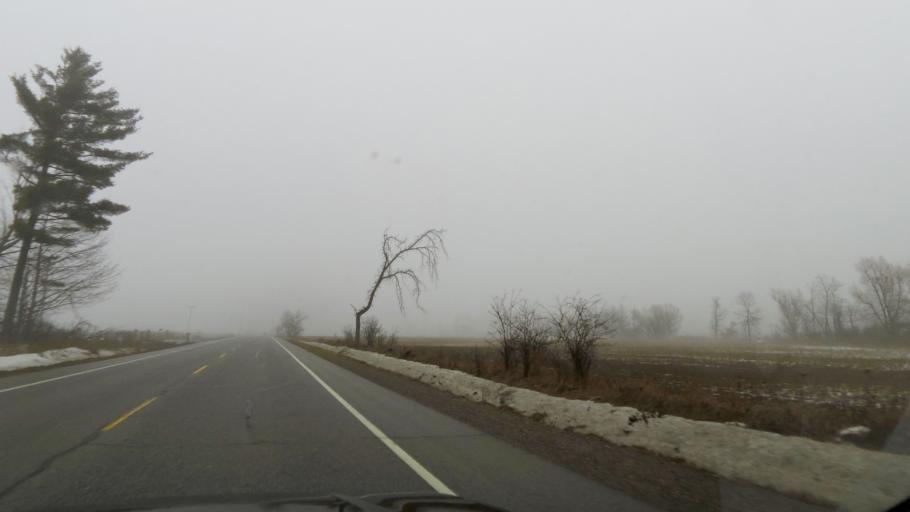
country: CA
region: Ontario
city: Brampton
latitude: 43.8460
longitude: -79.8650
